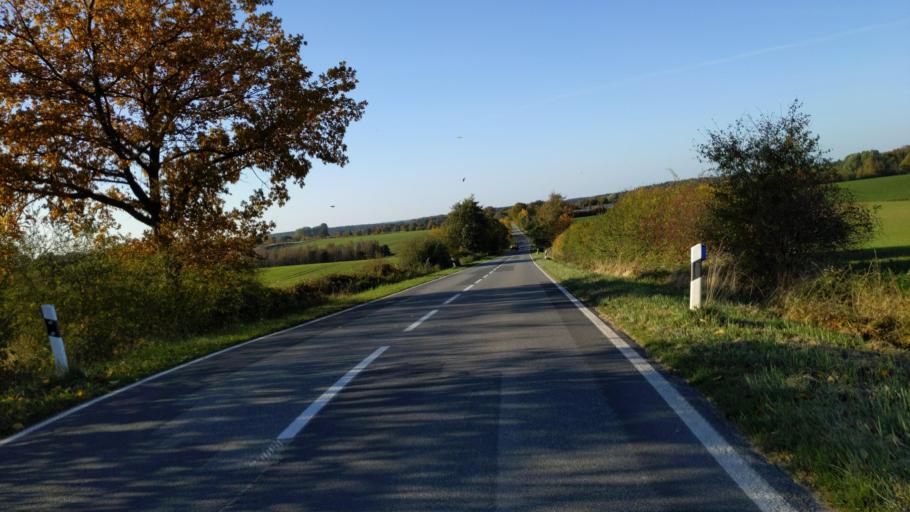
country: DE
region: Schleswig-Holstein
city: Gross Sarau
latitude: 53.7713
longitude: 10.7245
